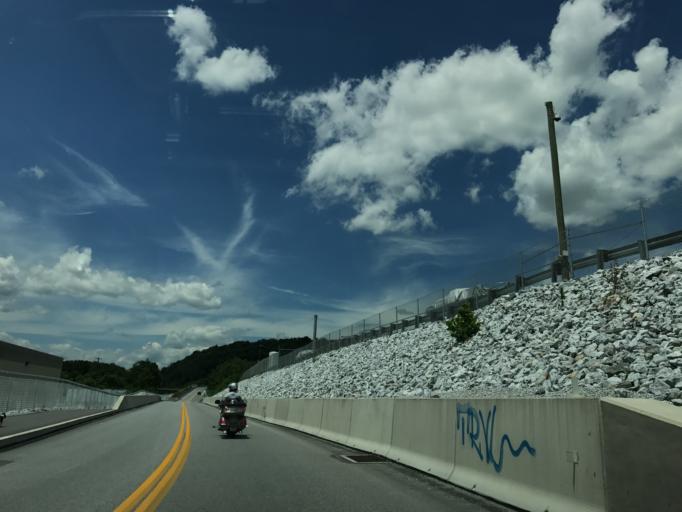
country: US
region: Pennsylvania
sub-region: Lancaster County
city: Columbia
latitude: 40.0336
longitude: -76.5084
